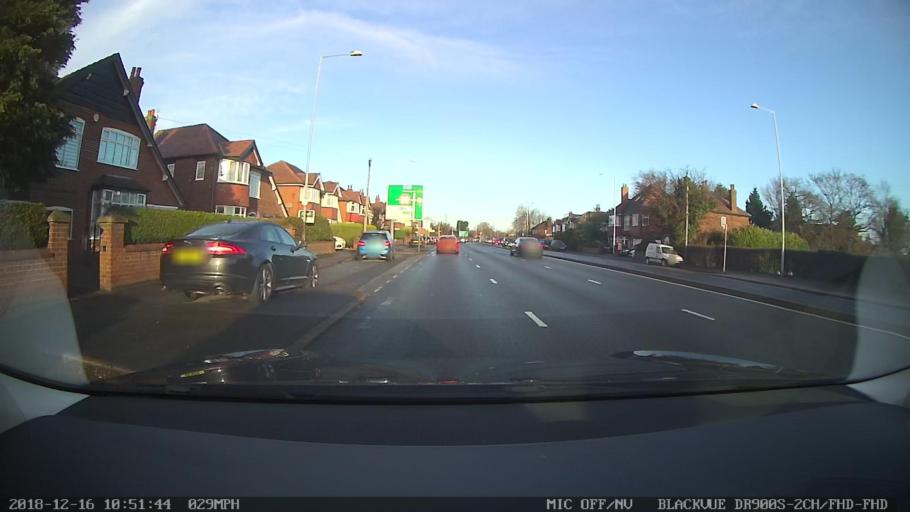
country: GB
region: England
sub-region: Manchester
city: Didsbury
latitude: 53.3903
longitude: -2.2262
